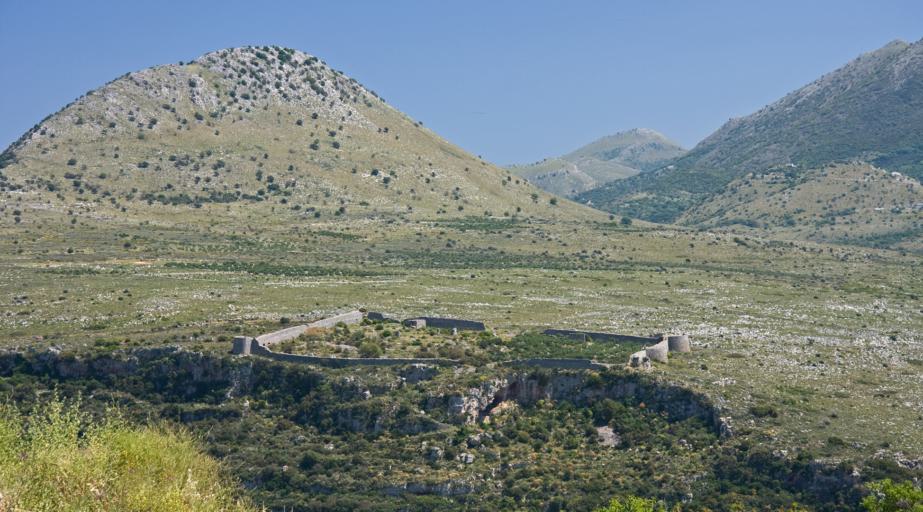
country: GR
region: Peloponnese
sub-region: Nomos Lakonias
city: Gytheio
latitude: 36.7081
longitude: 22.3832
